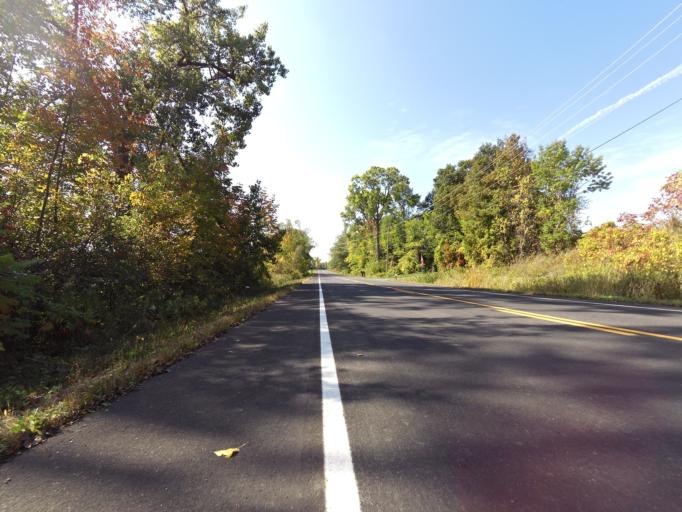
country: CA
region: Ontario
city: Picton
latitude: 44.0516
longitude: -77.0412
